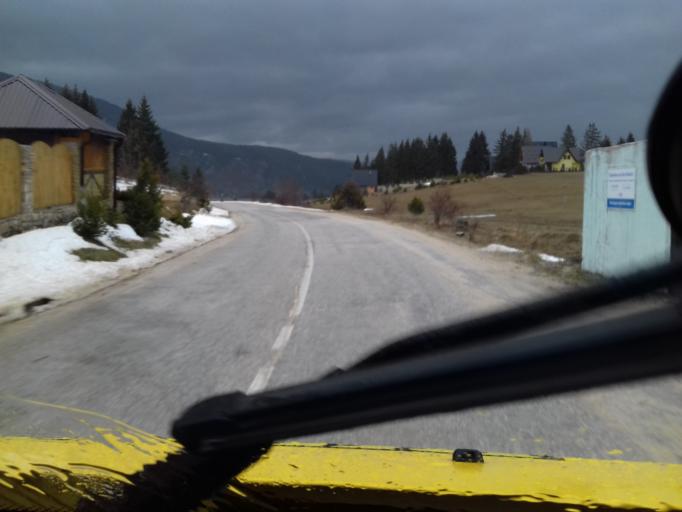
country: BA
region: Federation of Bosnia and Herzegovina
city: Turbe
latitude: 44.3151
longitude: 17.5537
